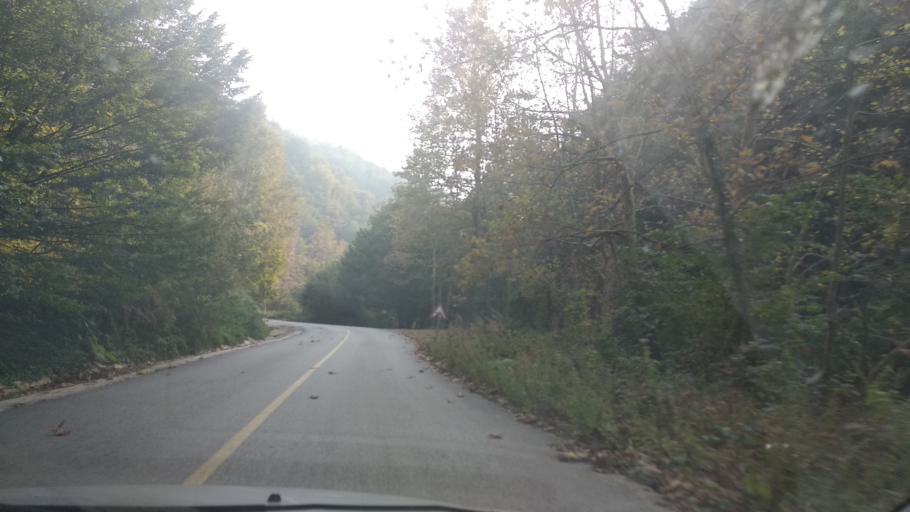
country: TR
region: Duzce
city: Kaynasli
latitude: 40.7117
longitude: 31.2665
